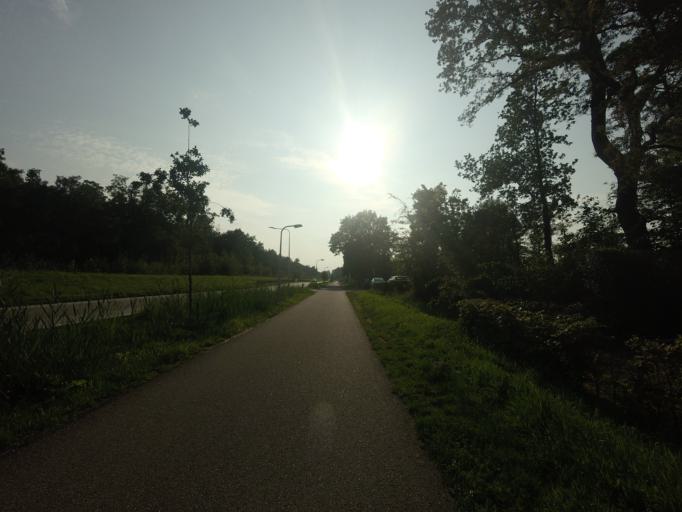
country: NL
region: Groningen
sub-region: Gemeente Haren
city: Haren
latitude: 53.1614
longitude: 6.5745
